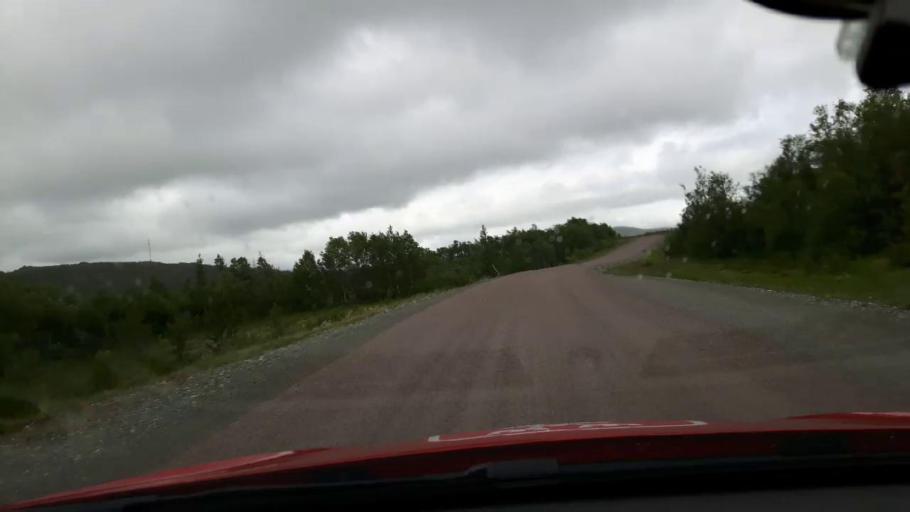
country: SE
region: Jaemtland
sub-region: Are Kommun
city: Are
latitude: 63.2492
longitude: 12.4279
